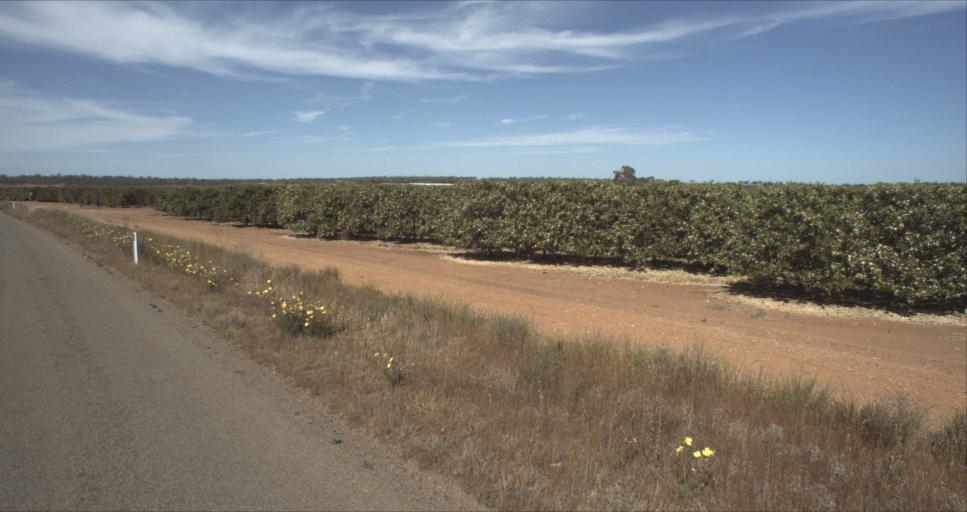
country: AU
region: New South Wales
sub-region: Leeton
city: Leeton
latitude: -34.5838
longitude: 146.4765
